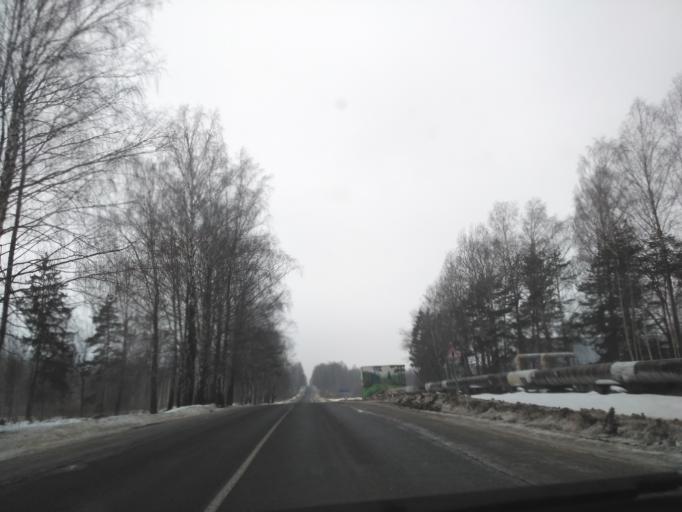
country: BY
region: Minsk
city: Horad Zhodzina
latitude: 54.0837
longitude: 28.3162
